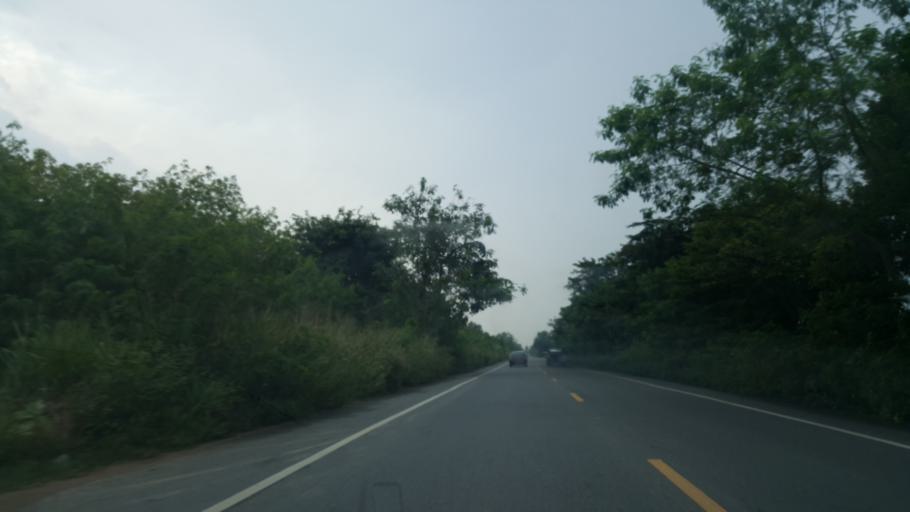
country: TH
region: Chon Buri
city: Sattahip
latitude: 12.7275
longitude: 100.9591
